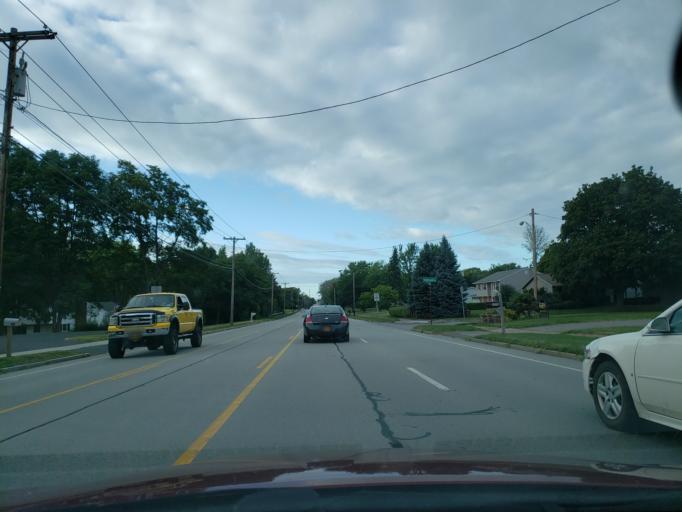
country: US
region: New York
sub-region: Monroe County
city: Greece
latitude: 43.2399
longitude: -77.6591
